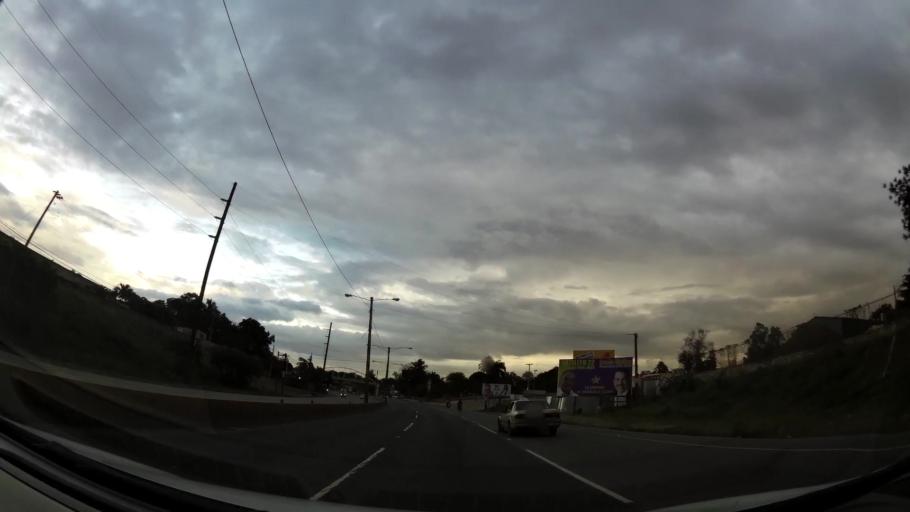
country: DO
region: Santo Domingo
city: Santo Domingo Oeste
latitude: 18.5516
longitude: -70.0544
